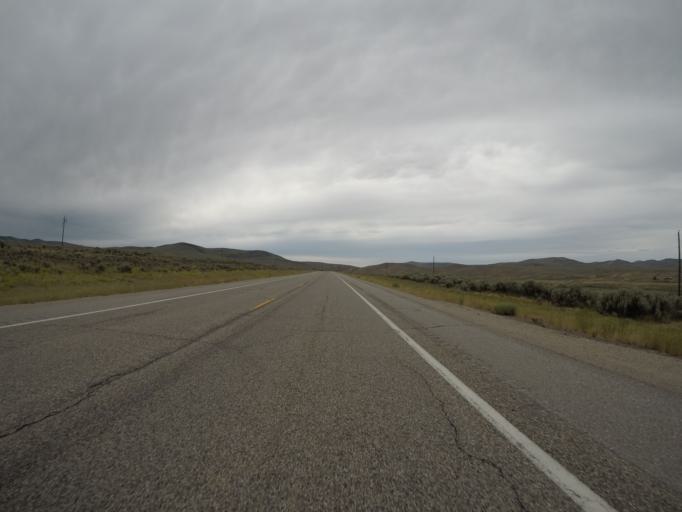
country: US
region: Wyoming
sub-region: Lincoln County
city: Kemmerer
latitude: 41.8168
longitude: -110.7699
